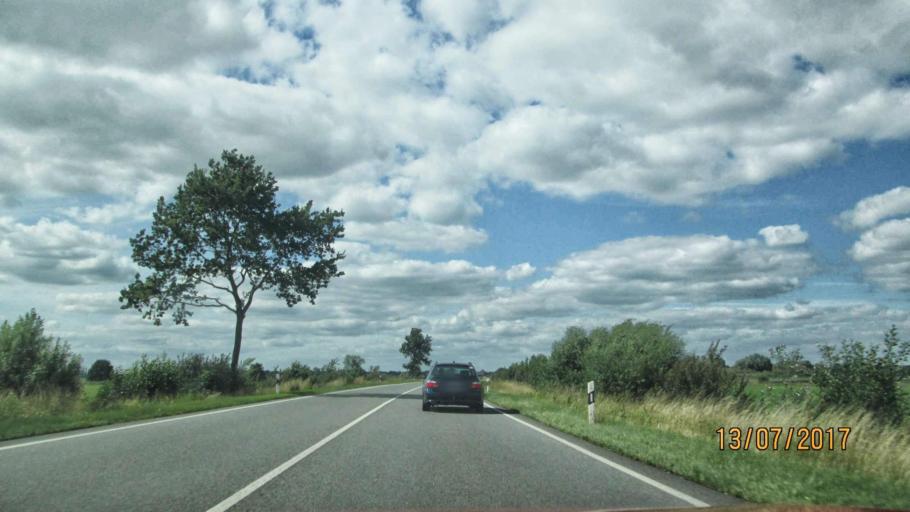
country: DE
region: Lower Saxony
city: Handorf
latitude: 53.3910
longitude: 10.3362
